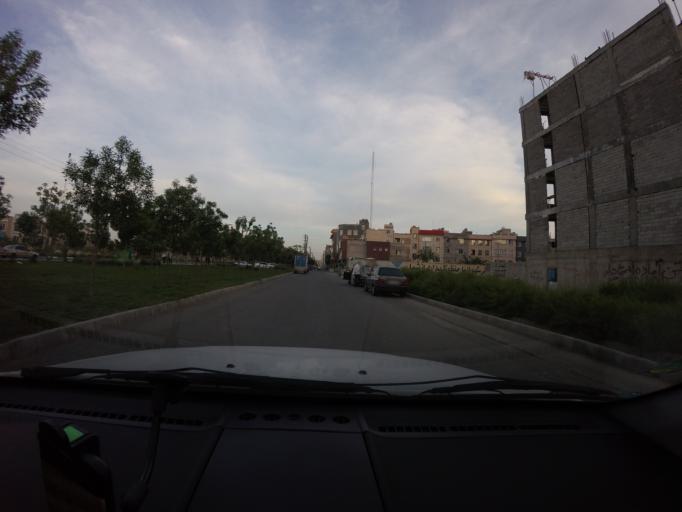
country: IR
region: Tehran
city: Eslamshahr
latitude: 35.5366
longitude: 51.2121
